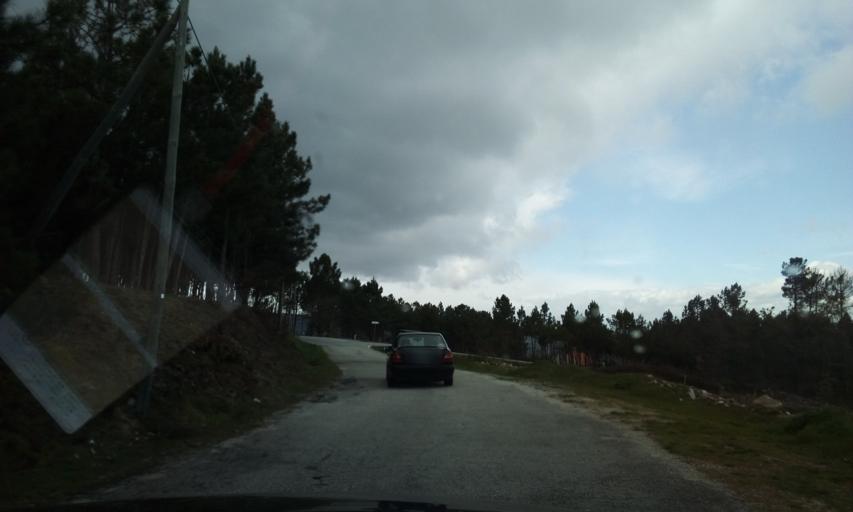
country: PT
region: Guarda
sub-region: Fornos de Algodres
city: Fornos de Algodres
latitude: 40.6371
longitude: -7.5781
